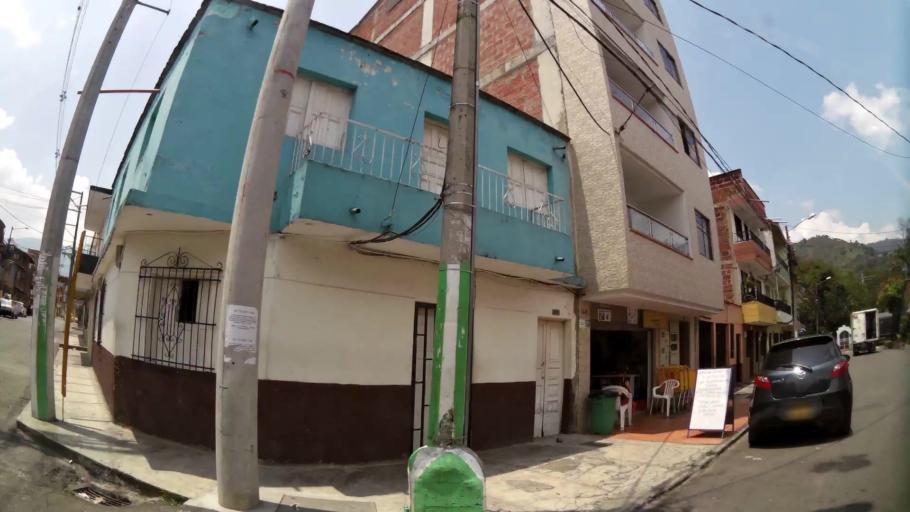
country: CO
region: Antioquia
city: Itagui
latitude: 6.1739
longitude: -75.6135
